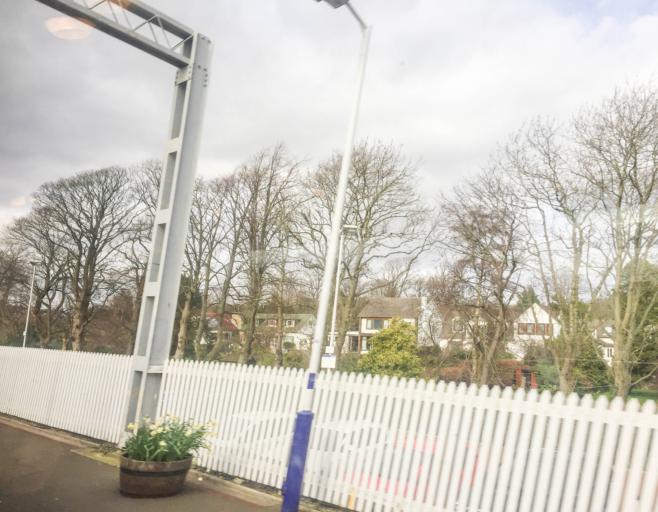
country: GB
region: Scotland
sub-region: Argyll and Bute
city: Cardross
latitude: 55.9601
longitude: -4.6523
